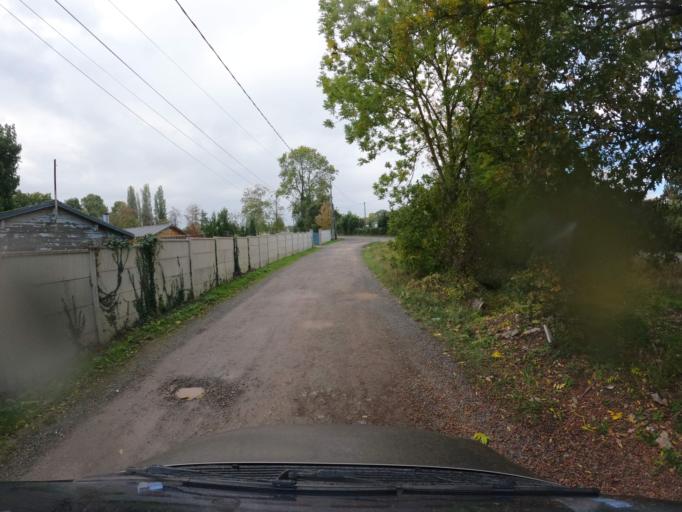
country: FR
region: Ile-de-France
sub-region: Departement de Seine-et-Marne
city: Saint-Germain-sur-Morin
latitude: 48.8724
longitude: 2.8534
